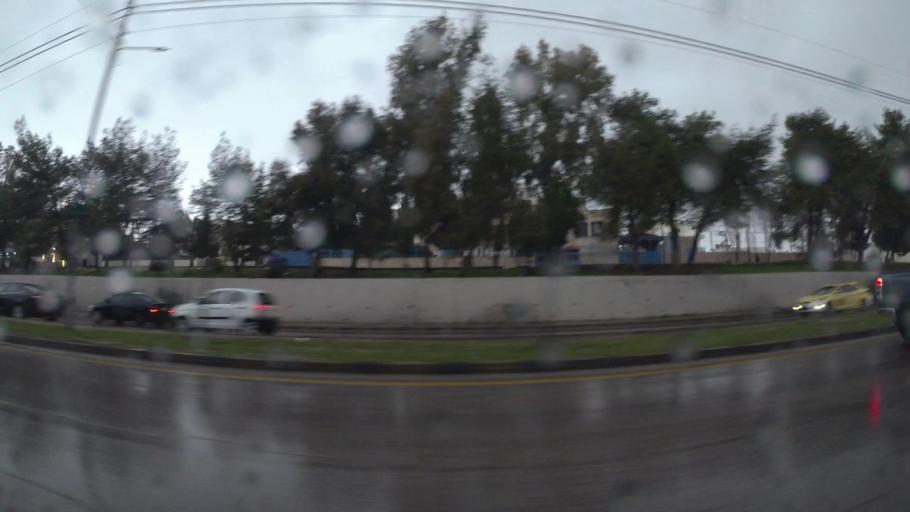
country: JO
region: Amman
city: Umm as Summaq
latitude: 31.9033
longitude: 35.8530
